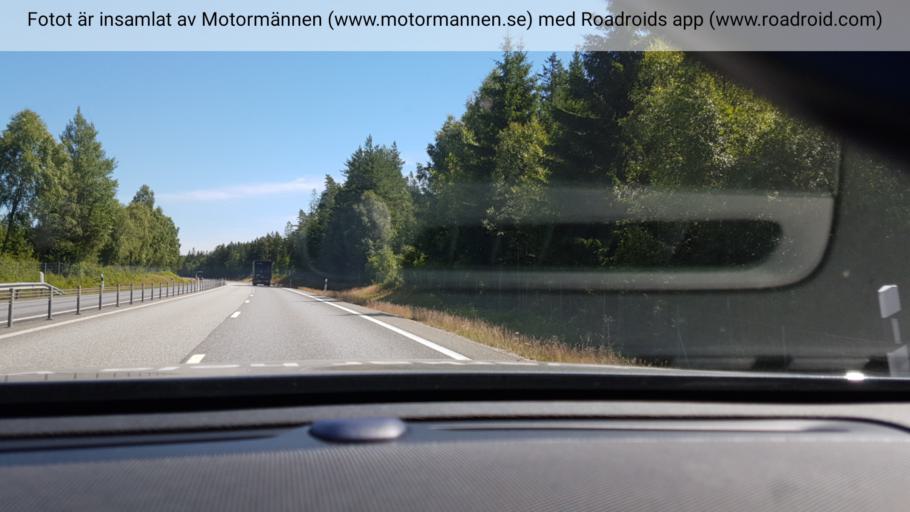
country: SE
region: Kronoberg
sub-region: Ljungby Kommun
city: Lagan
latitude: 56.8574
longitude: 14.1161
